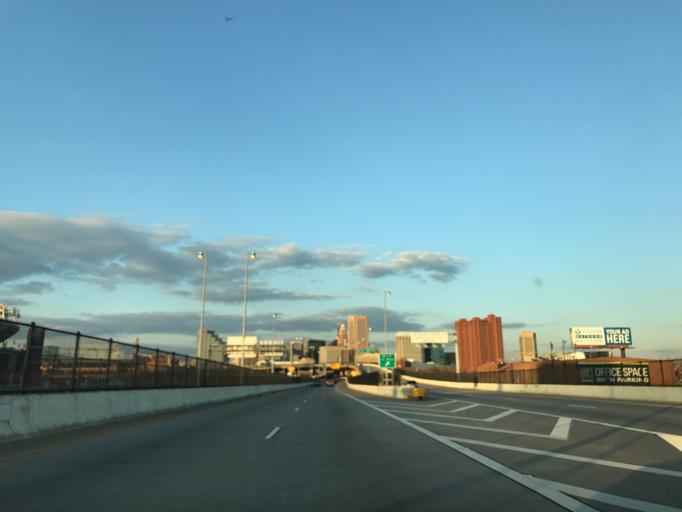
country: US
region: Maryland
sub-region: City of Baltimore
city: Baltimore
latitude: 39.2748
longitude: -76.6207
